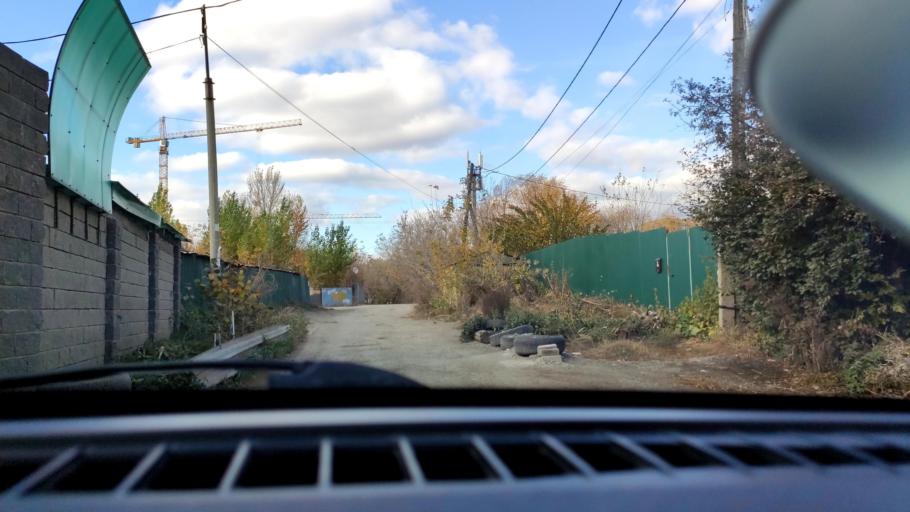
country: RU
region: Samara
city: Samara
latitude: 53.2218
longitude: 50.2087
